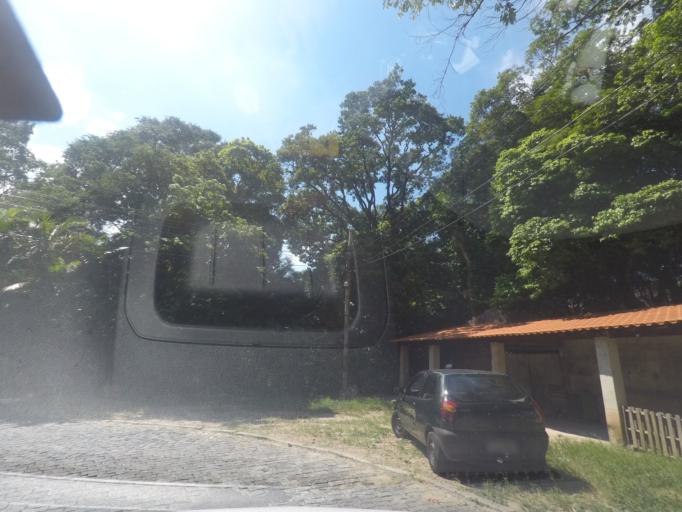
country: BR
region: Rio de Janeiro
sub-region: Petropolis
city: Petropolis
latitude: -22.5477
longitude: -43.1833
